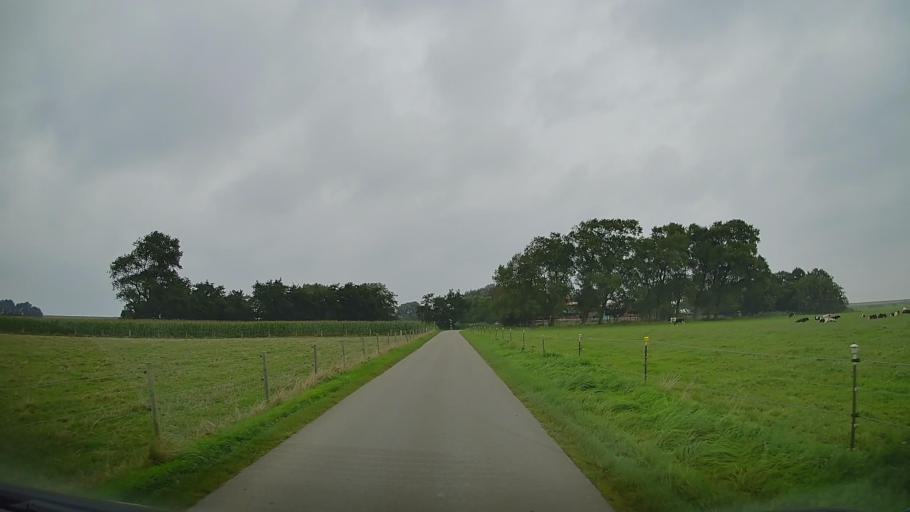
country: DE
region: Lower Saxony
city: Otterndorf
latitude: 53.8203
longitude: 8.9207
